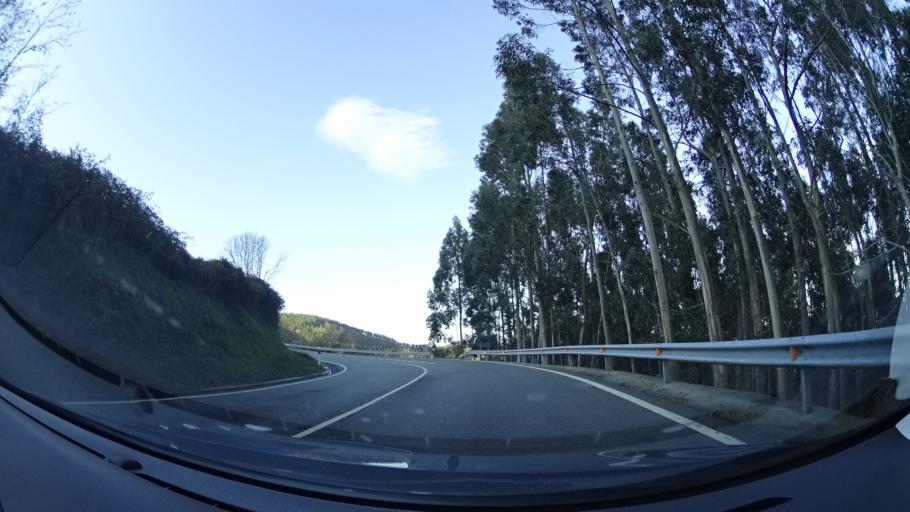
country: ES
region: Basque Country
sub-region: Bizkaia
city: Bermeo
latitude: 43.4092
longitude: -2.7622
